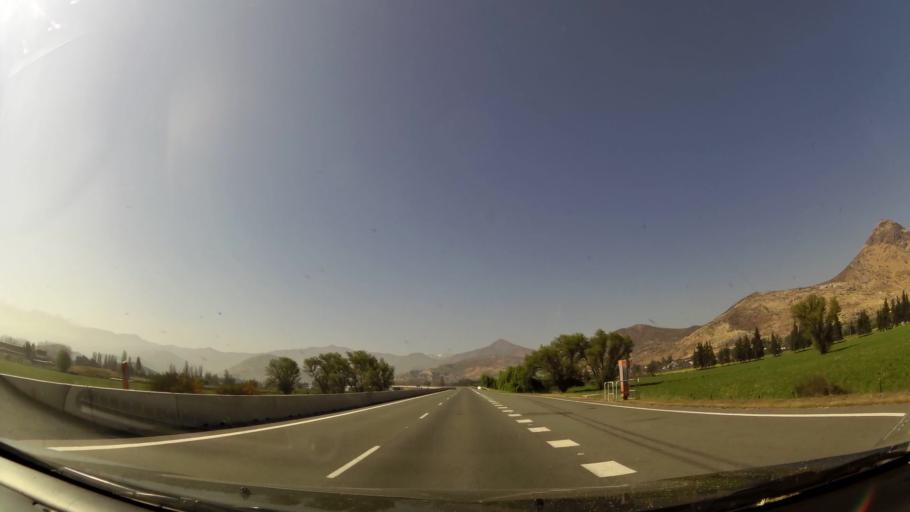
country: CL
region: Santiago Metropolitan
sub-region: Provincia de Chacabuco
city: Chicureo Abajo
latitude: -33.2957
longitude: -70.6888
